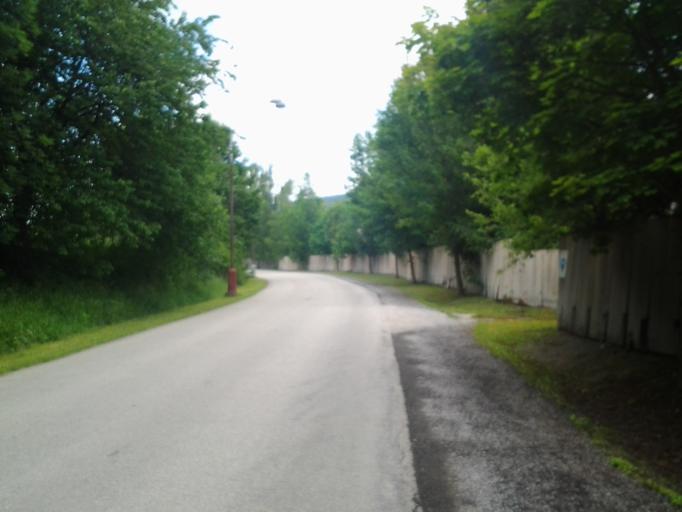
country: CZ
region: Jihocesky
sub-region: Okres Cesky Krumlov
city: Cesky Krumlov
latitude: 48.8268
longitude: 14.3074
